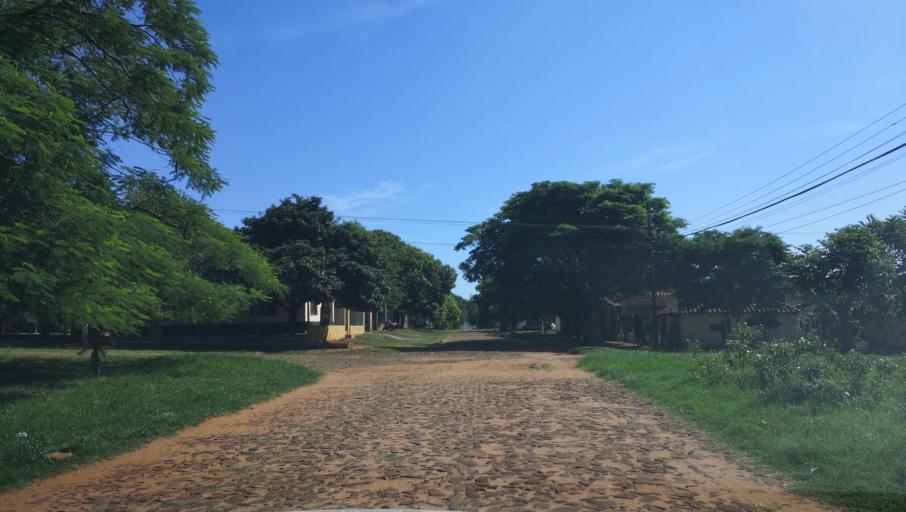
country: PY
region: Misiones
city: Santa Maria
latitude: -26.8966
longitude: -57.0259
